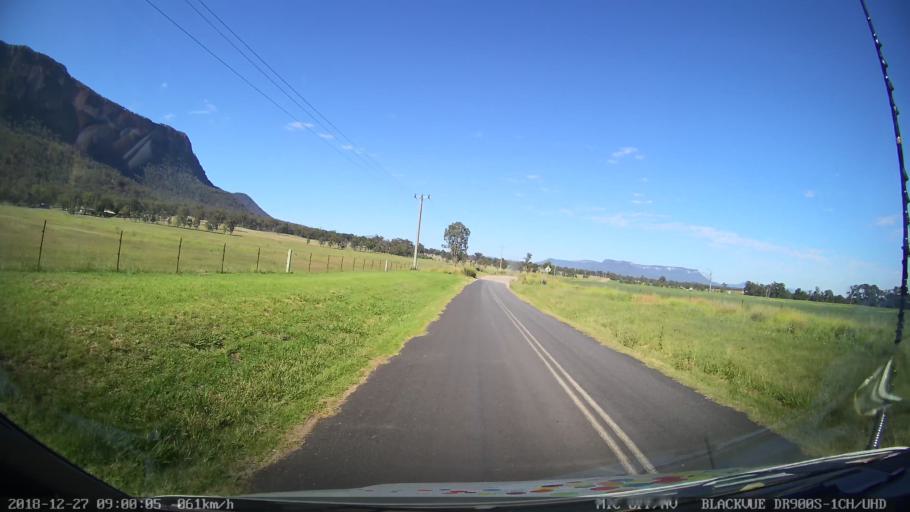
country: AU
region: New South Wales
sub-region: Mid-Western Regional
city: Kandos
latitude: -33.1007
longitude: 150.2303
